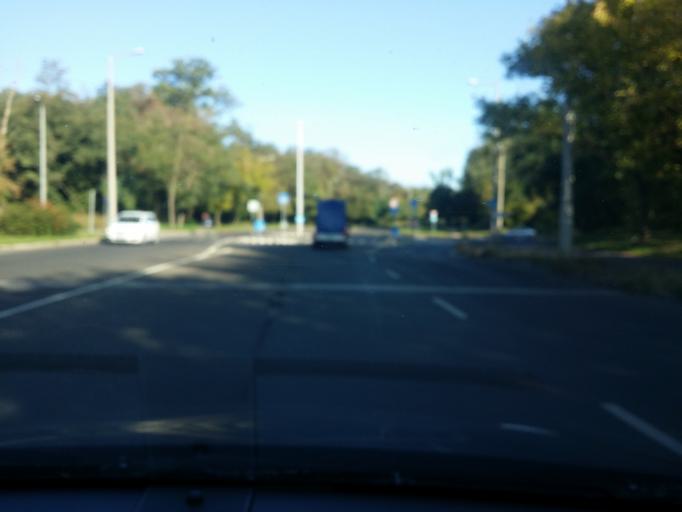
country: HU
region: Budapest
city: Budapest XV. keruelet
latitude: 47.5816
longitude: 19.1058
